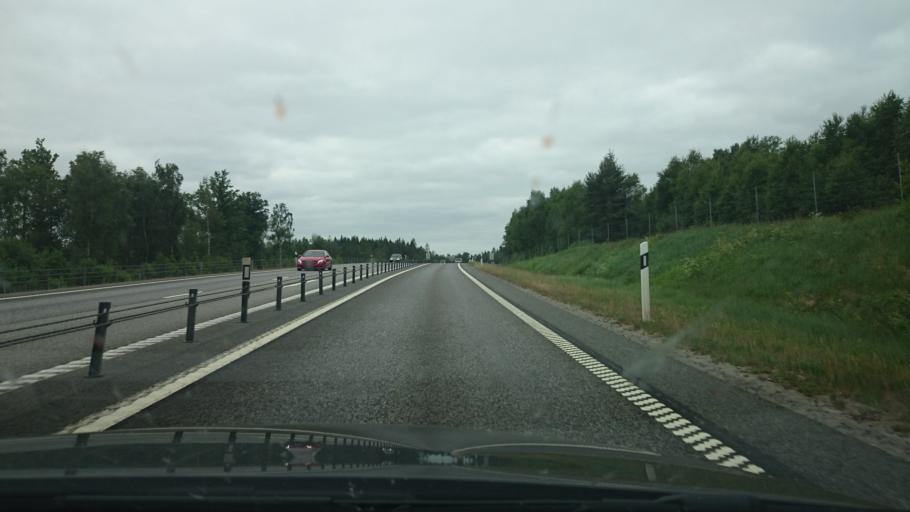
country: SE
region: Halland
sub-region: Hylte Kommun
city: Hyltebruk
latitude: 56.9833
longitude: 13.2111
